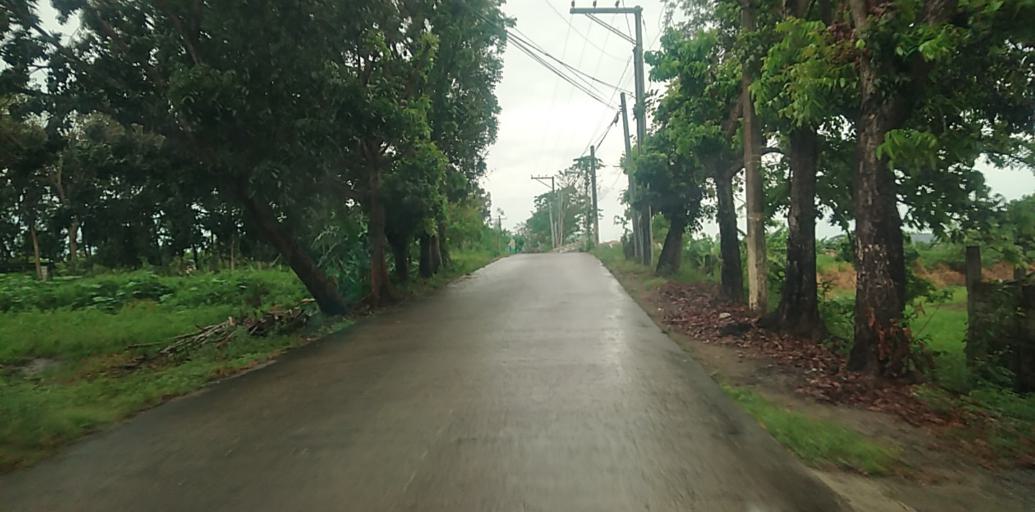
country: PH
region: Central Luzon
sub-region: Province of Pampanga
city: Arayat
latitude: 15.1425
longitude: 120.7394
